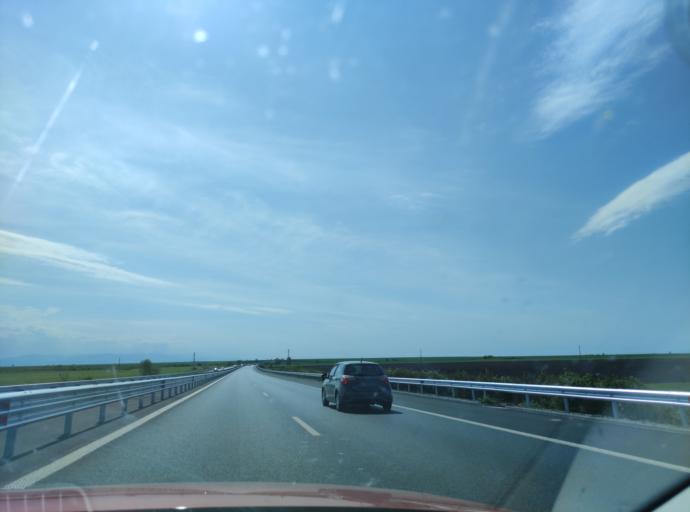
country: BG
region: Stara Zagora
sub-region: Obshtina Chirpan
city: Chirpan
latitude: 42.1995
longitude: 25.2751
